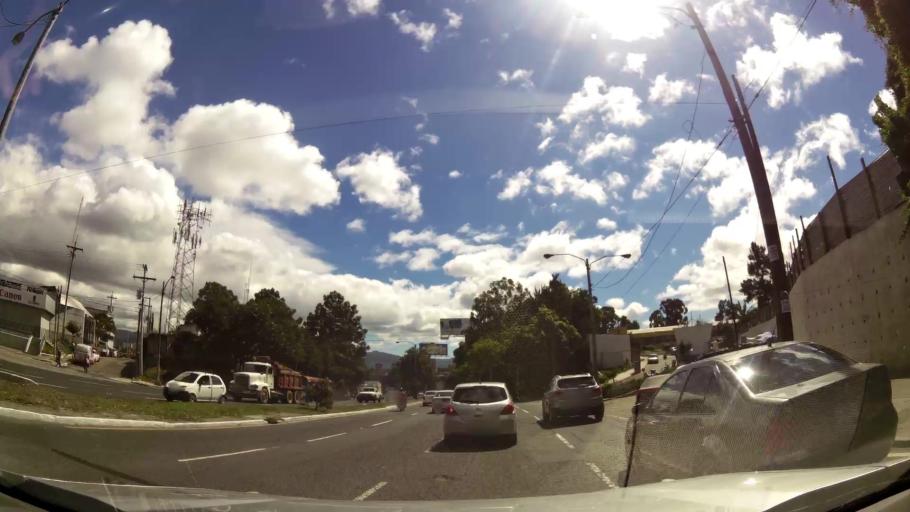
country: GT
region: Guatemala
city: Guatemala City
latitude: 14.6079
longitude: -90.5317
